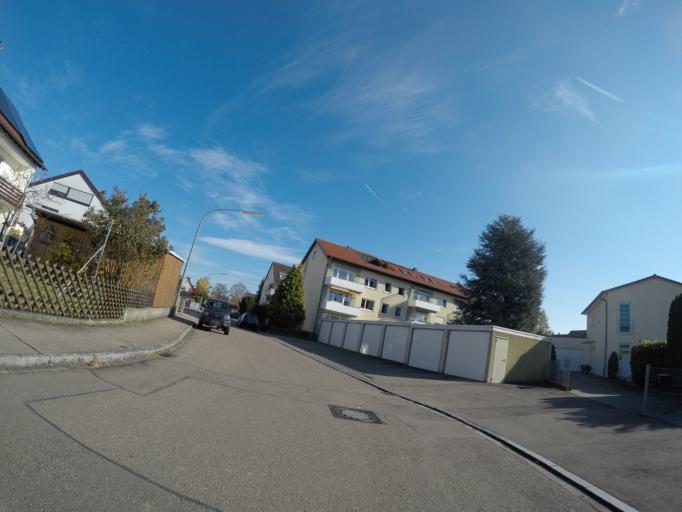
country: DE
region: Bavaria
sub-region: Swabia
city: Neu-Ulm
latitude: 48.4089
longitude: 10.0331
